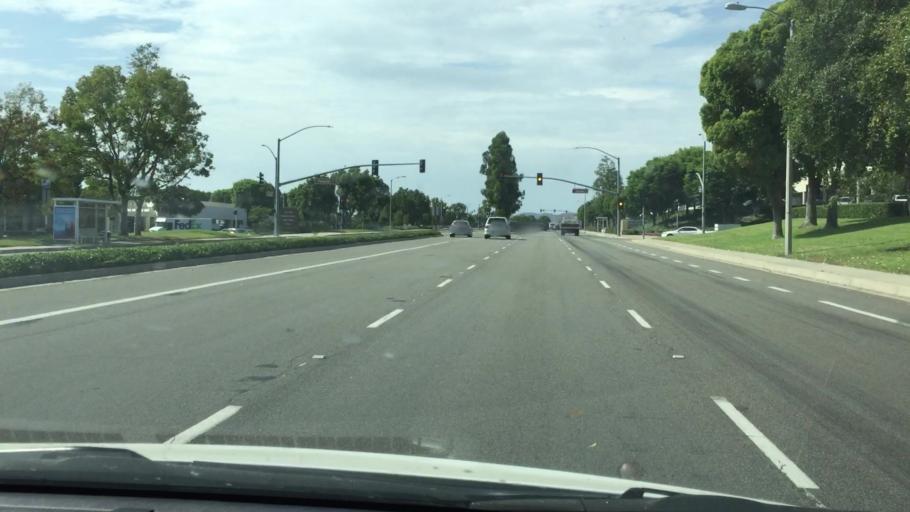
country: US
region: California
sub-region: Orange County
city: Lake Forest
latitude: 33.6603
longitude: -117.7056
